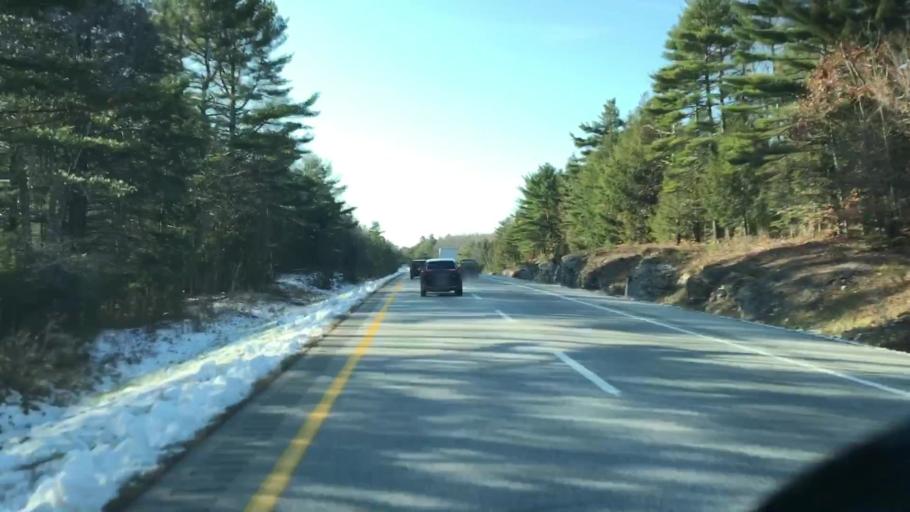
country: US
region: Maine
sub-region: Penobscot County
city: Etna
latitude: 44.7870
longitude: -69.1223
